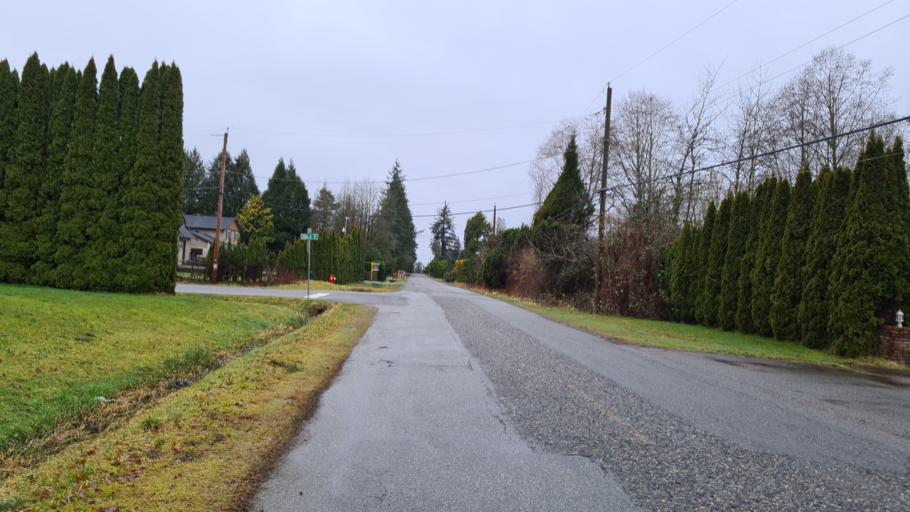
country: CA
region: British Columbia
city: Walnut Grove
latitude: 49.1383
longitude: -122.6492
